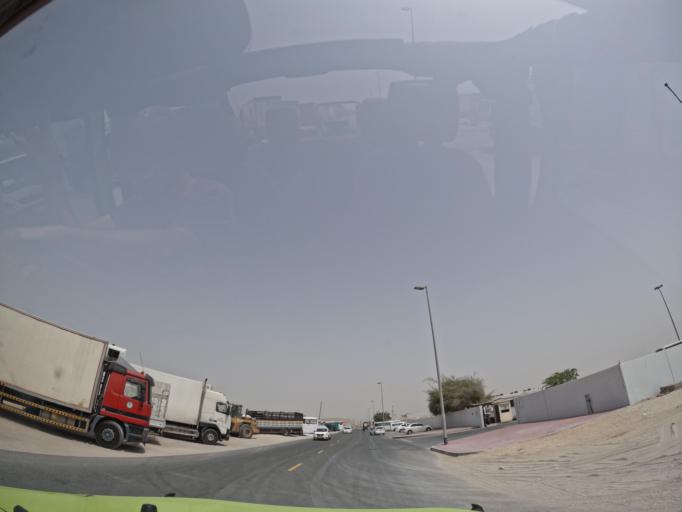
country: AE
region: Ash Shariqah
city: Sharjah
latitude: 25.1881
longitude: 55.3761
